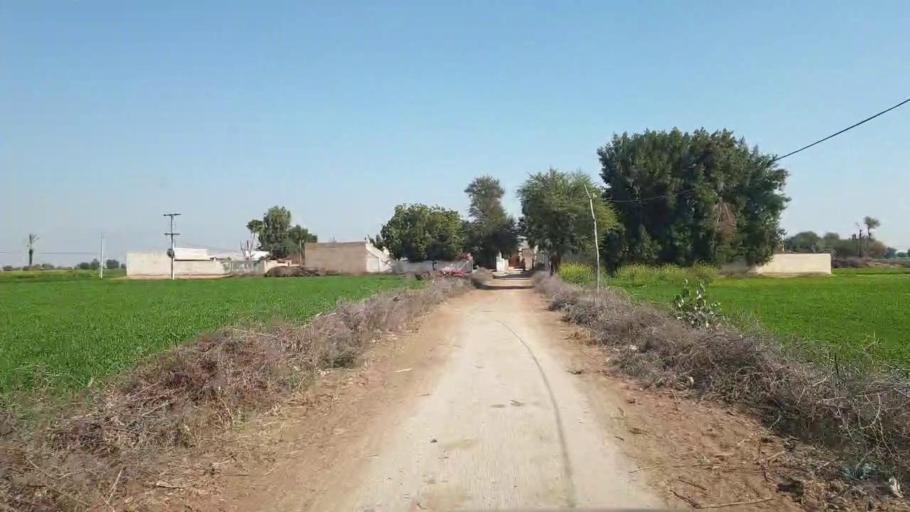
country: PK
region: Sindh
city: Shahpur Chakar
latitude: 26.1296
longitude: 68.6500
